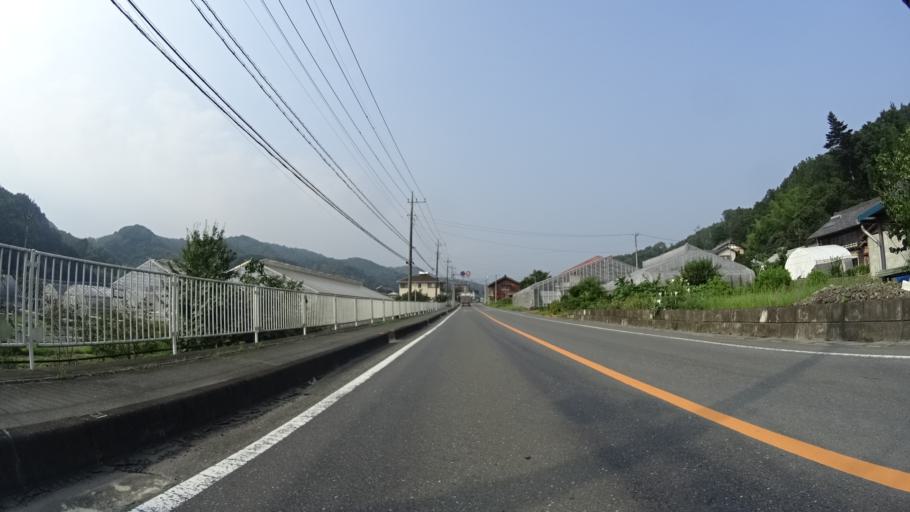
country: JP
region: Saitama
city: Chichibu
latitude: 36.0226
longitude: 139.0673
